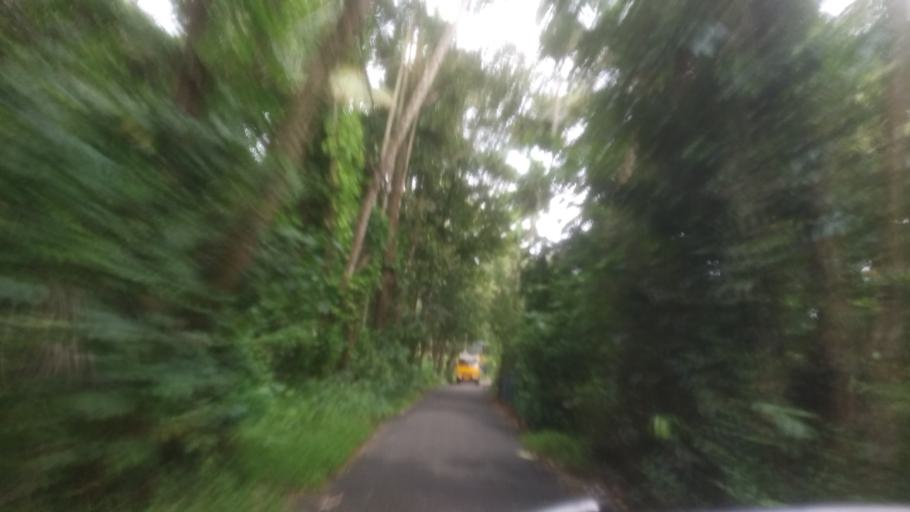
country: IN
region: Kerala
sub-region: Ernakulam
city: Elur
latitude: 10.0850
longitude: 76.2047
